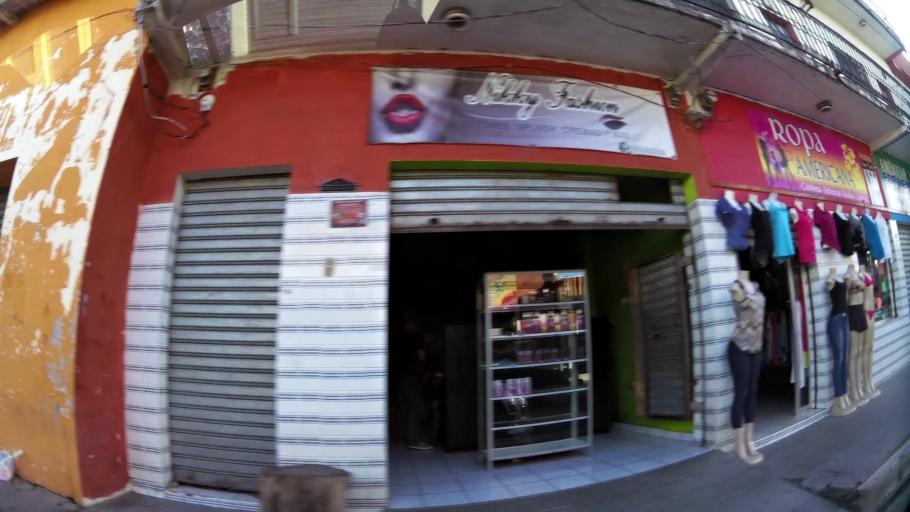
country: SV
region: Santa Ana
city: Metapan
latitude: 14.3306
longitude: -89.4445
